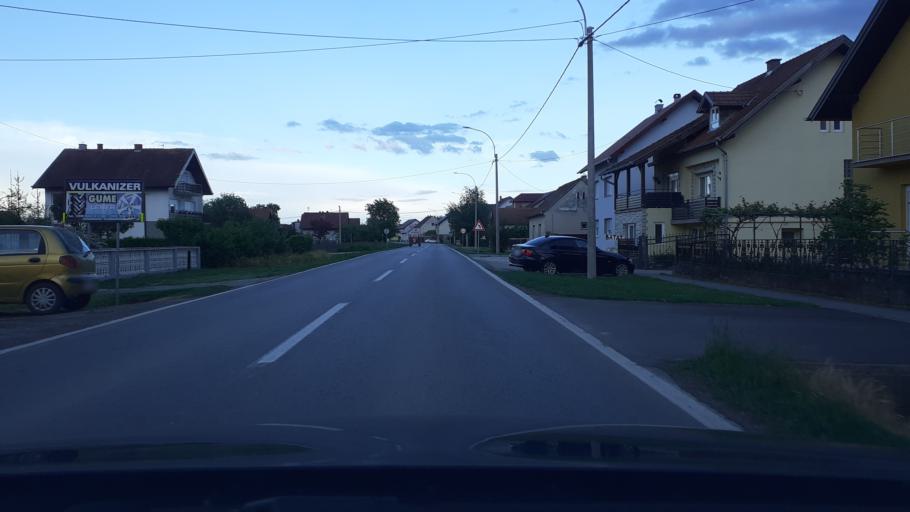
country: HR
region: Pozesko-Slavonska
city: Jaksic
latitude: 45.3576
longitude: 17.7680
